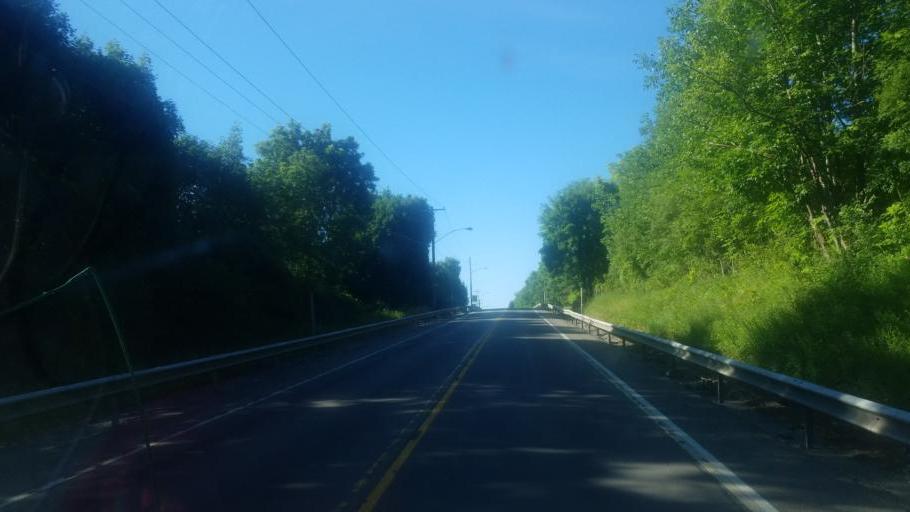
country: US
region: New York
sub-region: Wayne County
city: Newark
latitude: 43.0316
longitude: -77.0968
